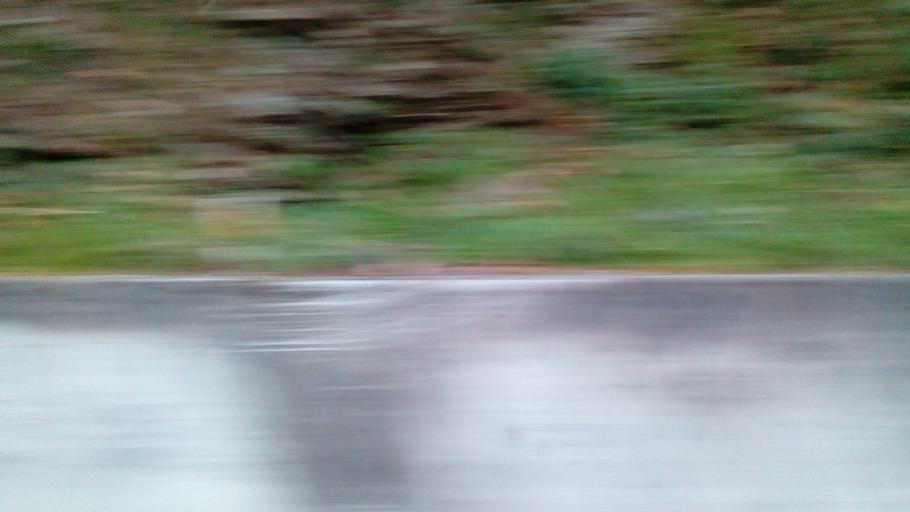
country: TW
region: Taiwan
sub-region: Hualien
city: Hualian
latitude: 24.3840
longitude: 121.3472
